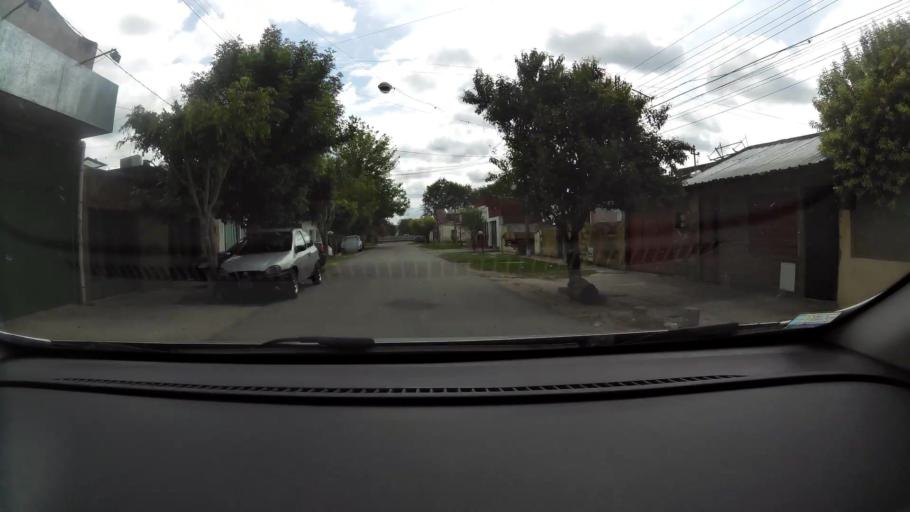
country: AR
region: Santa Fe
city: Gobernador Galvez
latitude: -33.0140
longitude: -60.6460
